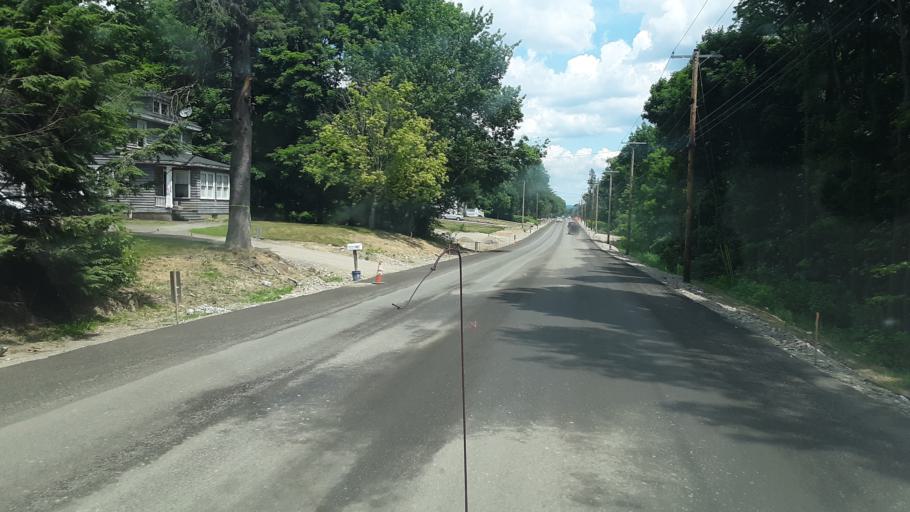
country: US
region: Maine
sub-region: Penobscot County
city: Hampden
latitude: 44.7592
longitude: -68.8138
